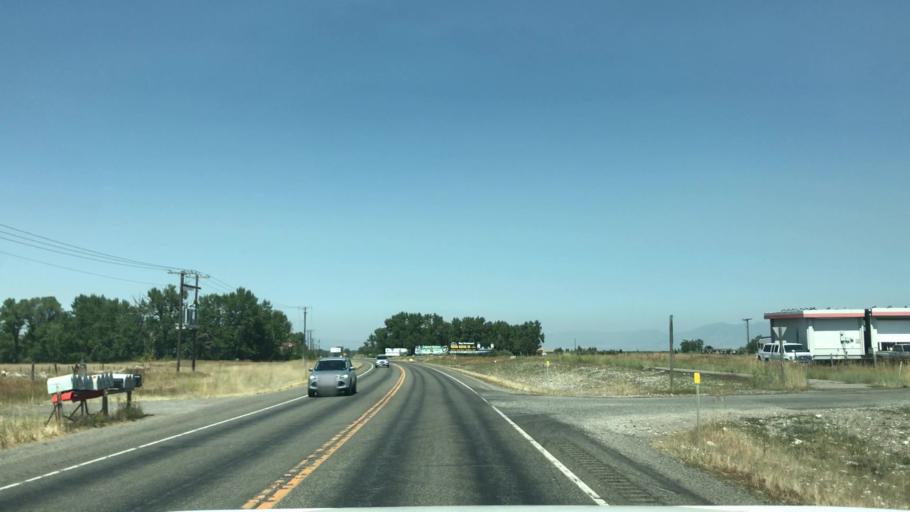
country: US
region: Montana
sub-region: Gallatin County
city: Four Corners
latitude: 45.6071
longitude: -111.1958
